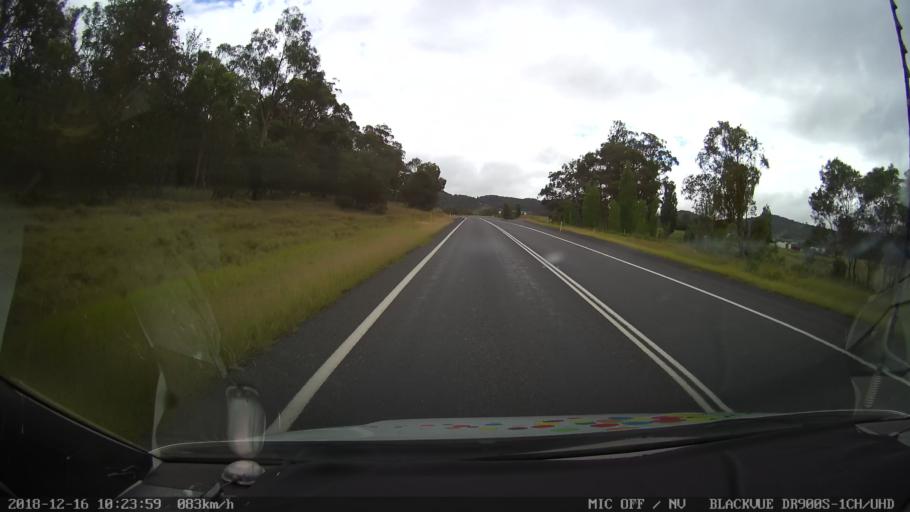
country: AU
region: New South Wales
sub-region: Tenterfield Municipality
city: Carrolls Creek
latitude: -29.1760
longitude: 152.0060
